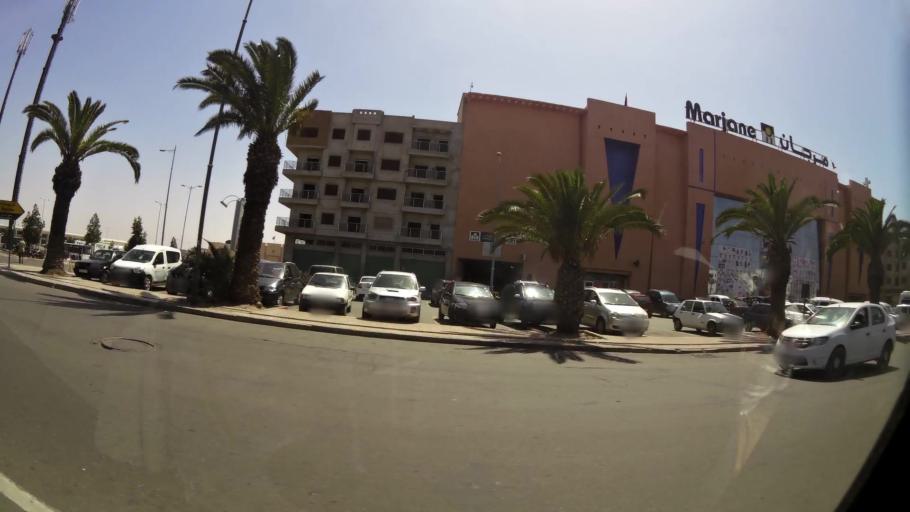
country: MA
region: Souss-Massa-Draa
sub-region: Inezgane-Ait Mellou
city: Inezgane
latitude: 30.3598
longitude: -9.5247
